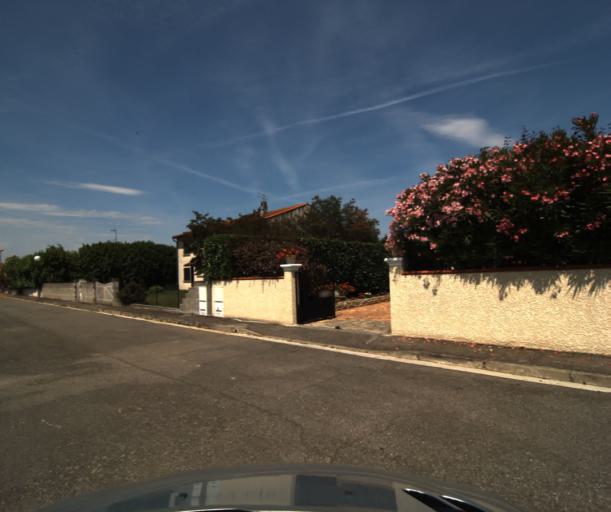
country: FR
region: Midi-Pyrenees
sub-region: Departement de la Haute-Garonne
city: Labastidette
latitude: 43.4588
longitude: 1.2467
